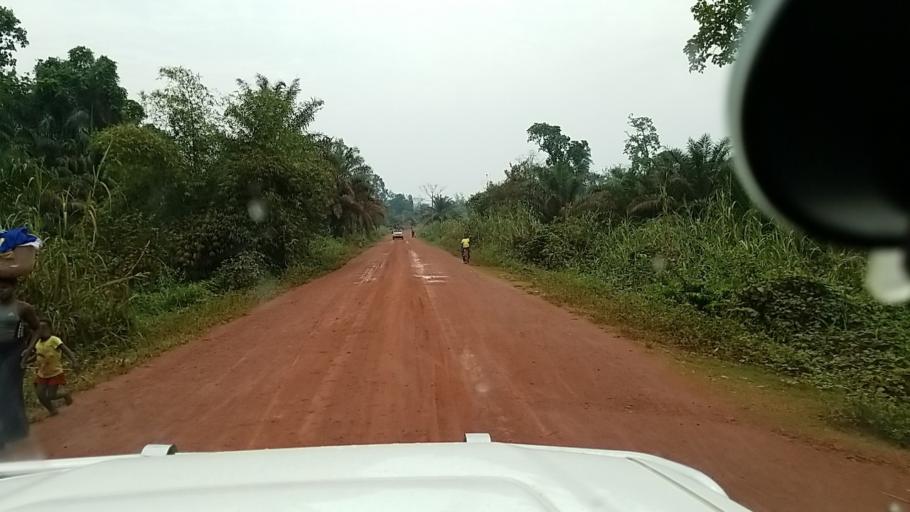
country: CD
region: Equateur
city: Gemena
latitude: 3.1340
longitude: 19.8208
